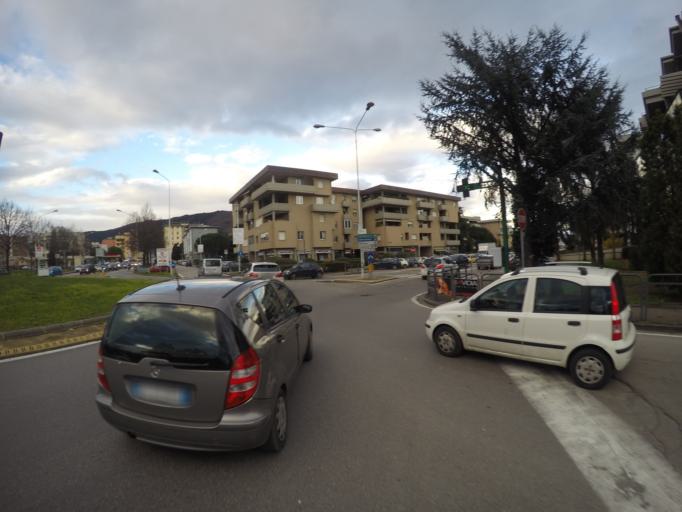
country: IT
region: Tuscany
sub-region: Provincia di Prato
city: Prato
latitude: 43.8640
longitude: 11.1105
